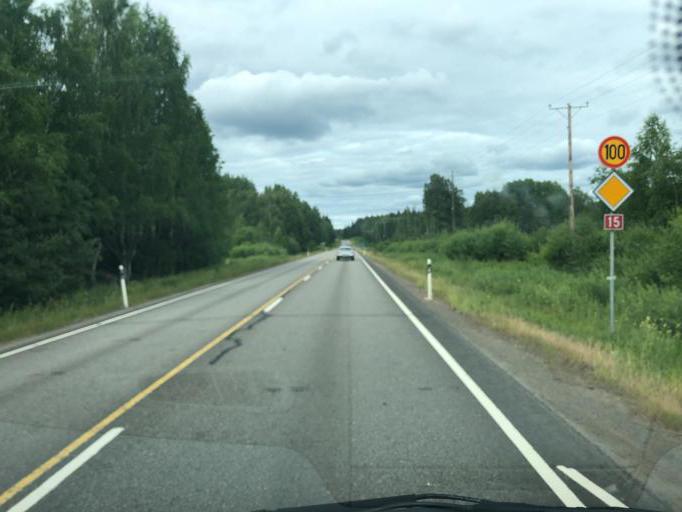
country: FI
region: Kymenlaakso
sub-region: Kouvola
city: Kouvola
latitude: 60.9801
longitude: 26.9086
